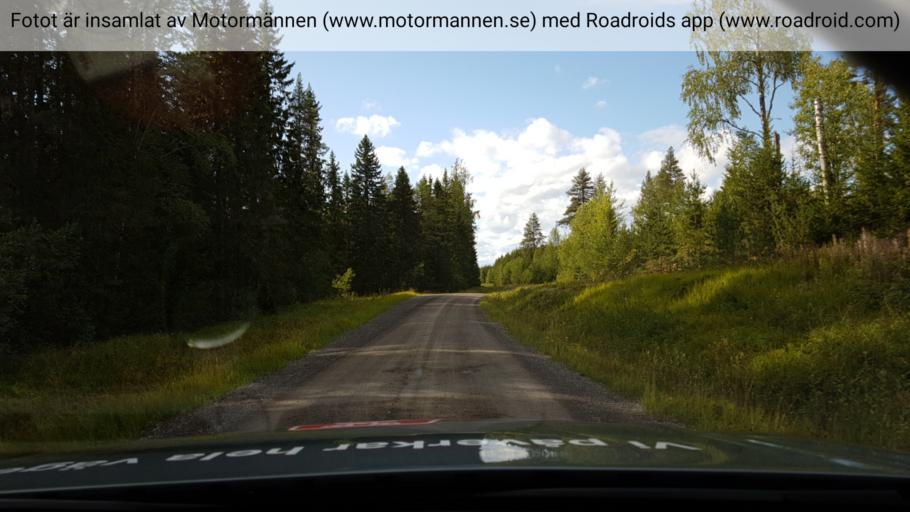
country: SE
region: Jaemtland
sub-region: OEstersunds Kommun
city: Lit
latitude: 63.3188
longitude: 15.2306
